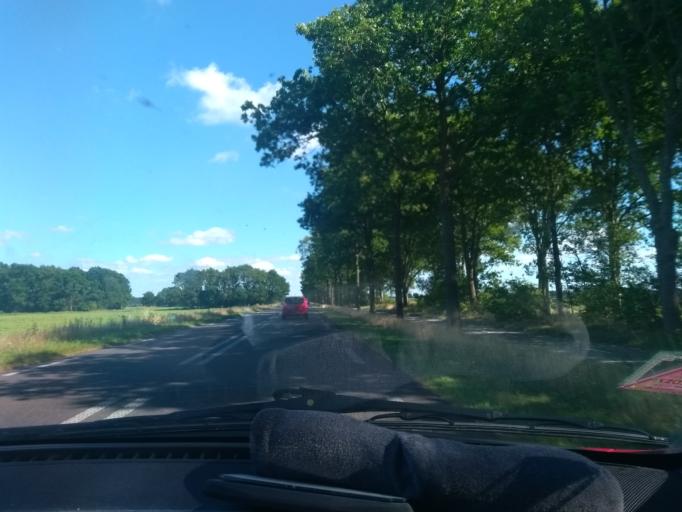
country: NL
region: Drenthe
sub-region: Gemeente Tynaarlo
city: Vries
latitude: 53.1172
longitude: 6.5111
